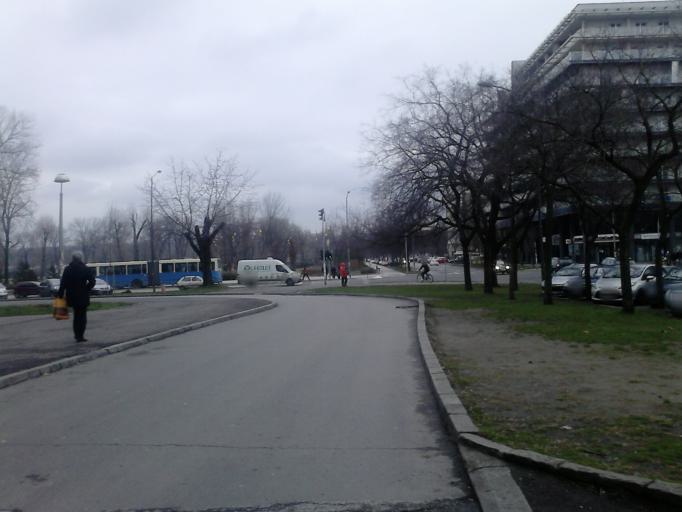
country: RS
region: Autonomna Pokrajina Vojvodina
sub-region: Juznobacki Okrug
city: Novi Sad
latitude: 45.2412
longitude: 19.8377
